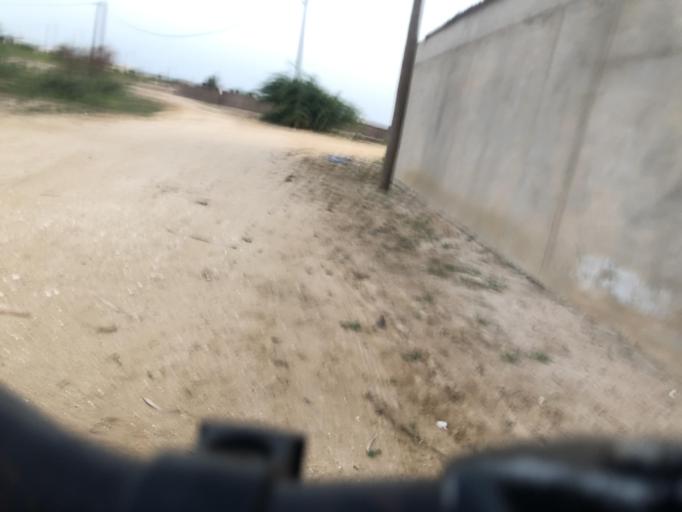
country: SN
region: Saint-Louis
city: Saint-Louis
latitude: 16.0727
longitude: -16.4341
